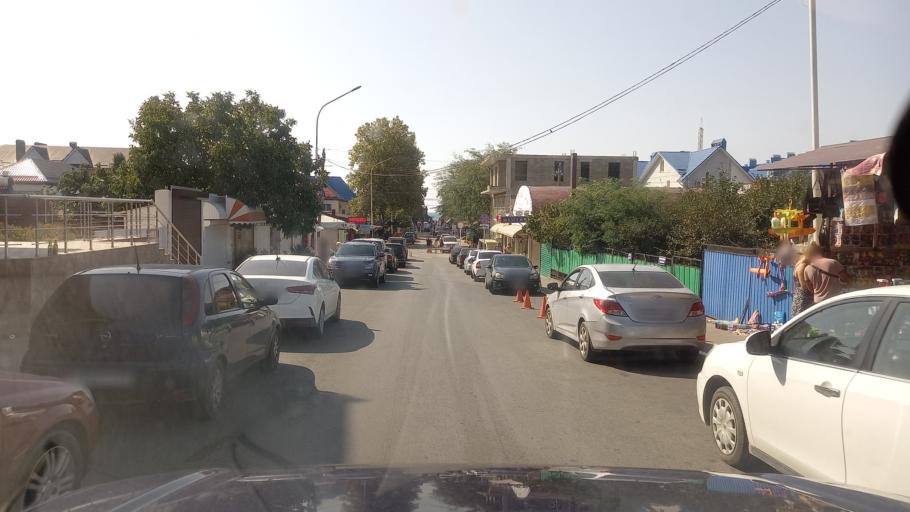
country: RU
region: Krasnodarskiy
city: Arkhipo-Osipovka
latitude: 44.3612
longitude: 38.5324
